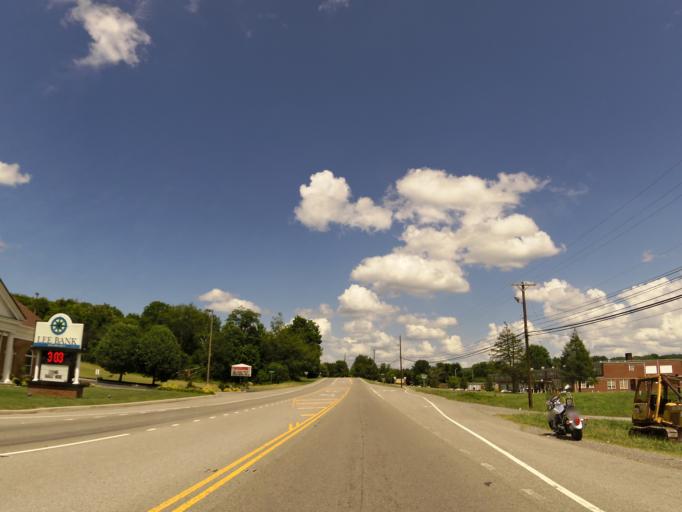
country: US
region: Virginia
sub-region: Lee County
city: Jonesville
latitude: 36.6845
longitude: -83.1259
